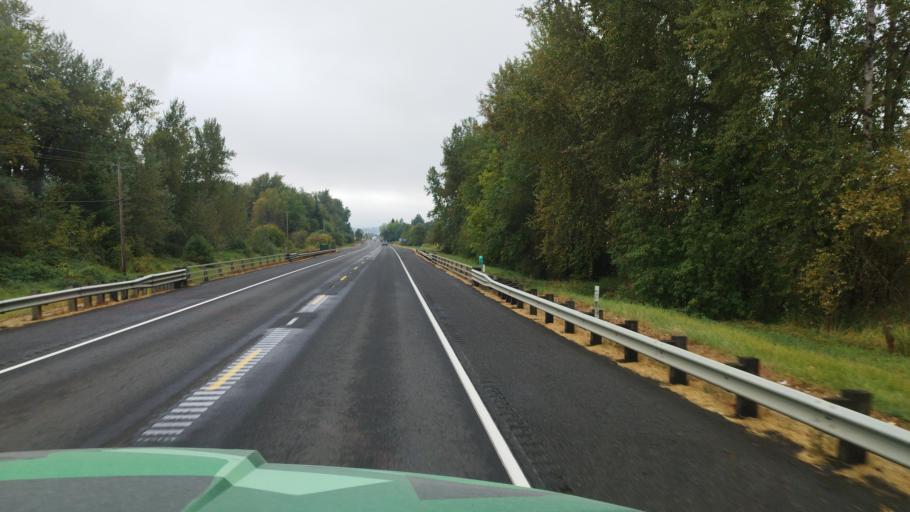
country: US
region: Oregon
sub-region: Washington County
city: Forest Grove
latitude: 45.4447
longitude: -123.1418
